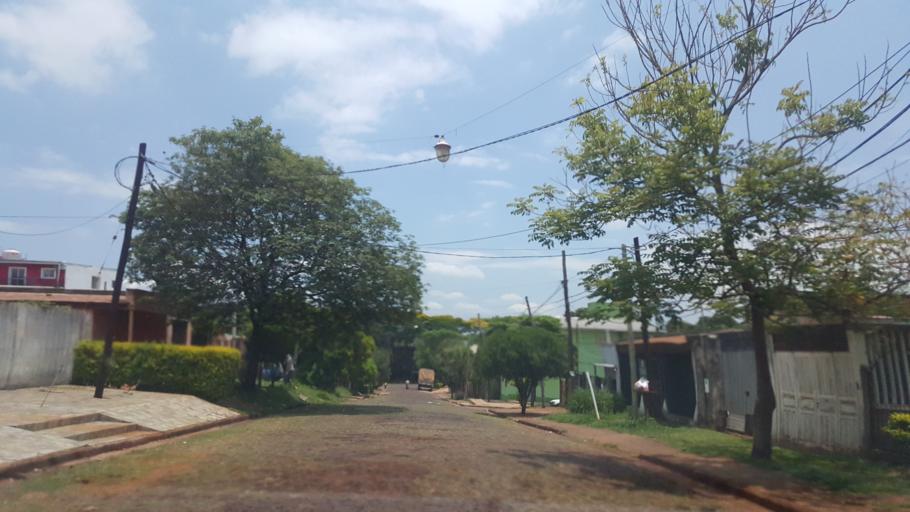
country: AR
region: Misiones
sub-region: Departamento de Capital
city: Posadas
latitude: -27.3923
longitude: -55.9058
